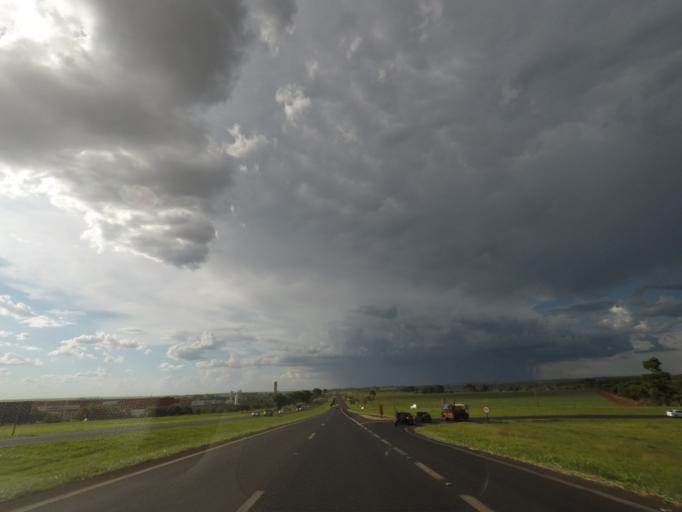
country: BR
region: Sao Paulo
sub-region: Jardinopolis
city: Jardinopolis
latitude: -21.0922
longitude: -47.7949
